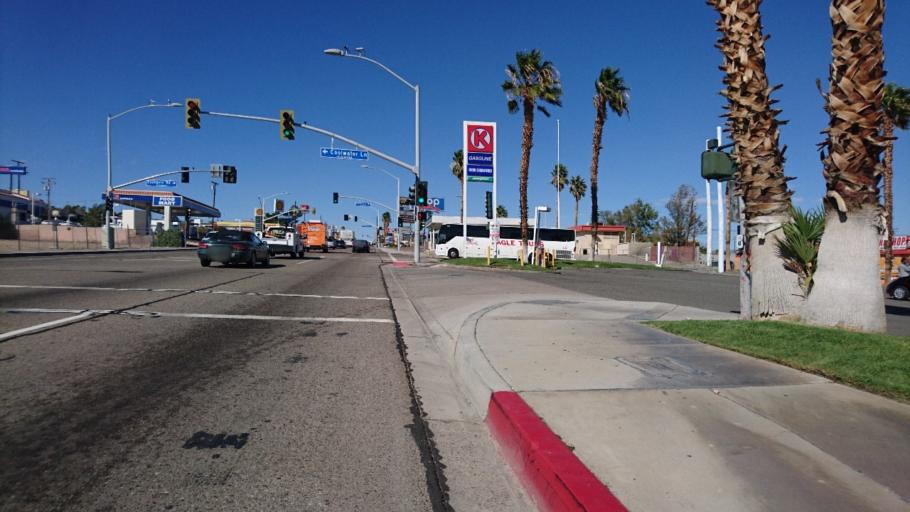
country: US
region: California
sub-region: San Bernardino County
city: Barstow
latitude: 34.8939
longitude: -117.0036
